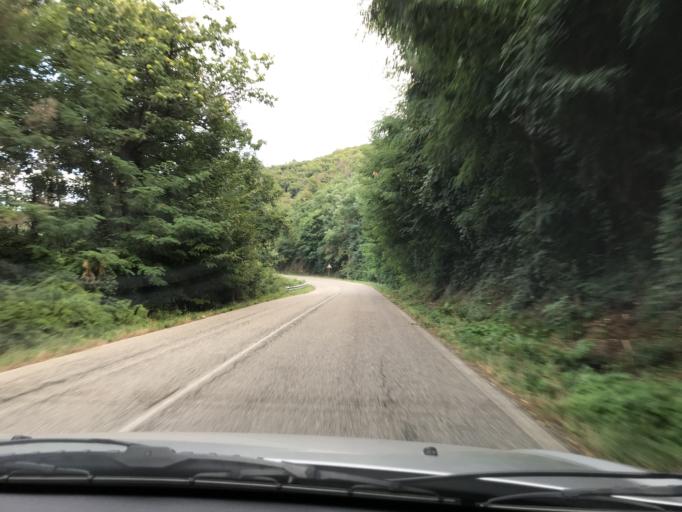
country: IT
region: Umbria
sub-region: Provincia di Terni
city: Montecchio
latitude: 42.6570
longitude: 12.3412
